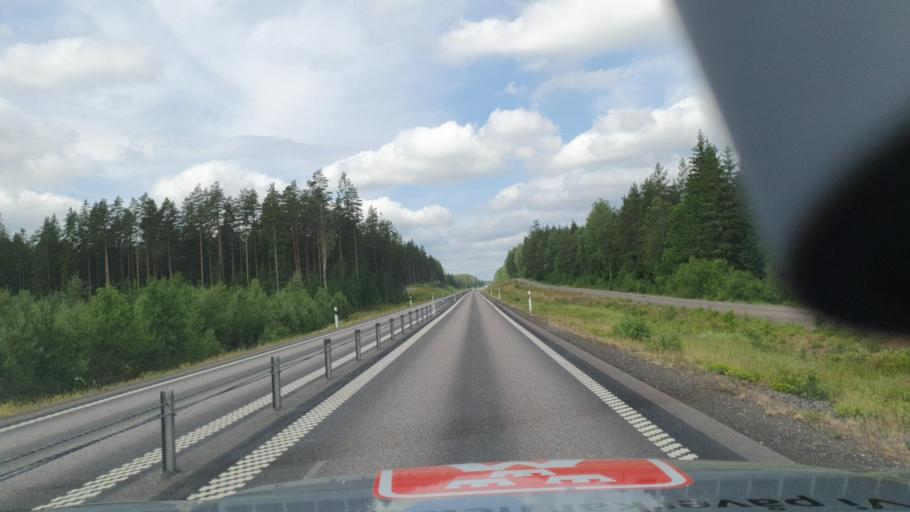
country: SE
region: Kalmar
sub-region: Emmaboda Kommun
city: Emmaboda
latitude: 56.7217
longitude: 15.6115
